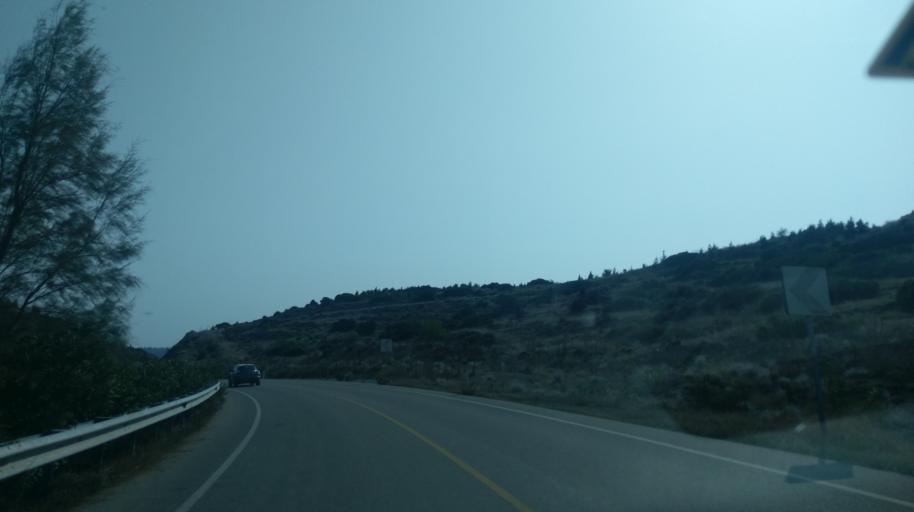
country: CY
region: Ammochostos
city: Leonarisso
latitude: 35.4825
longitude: 34.1045
